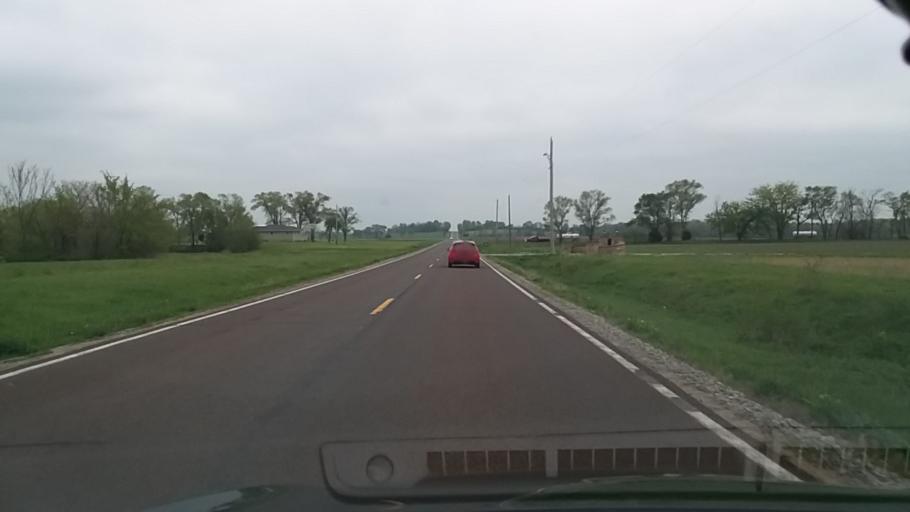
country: US
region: Kansas
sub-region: Douglas County
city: Eudora
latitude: 38.8531
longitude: -95.0932
